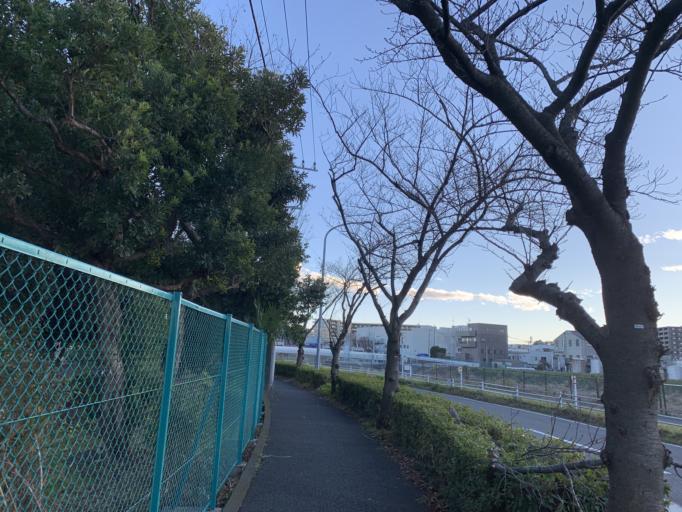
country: JP
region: Tokyo
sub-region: Machida-shi
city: Machida
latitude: 35.5152
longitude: 139.5516
